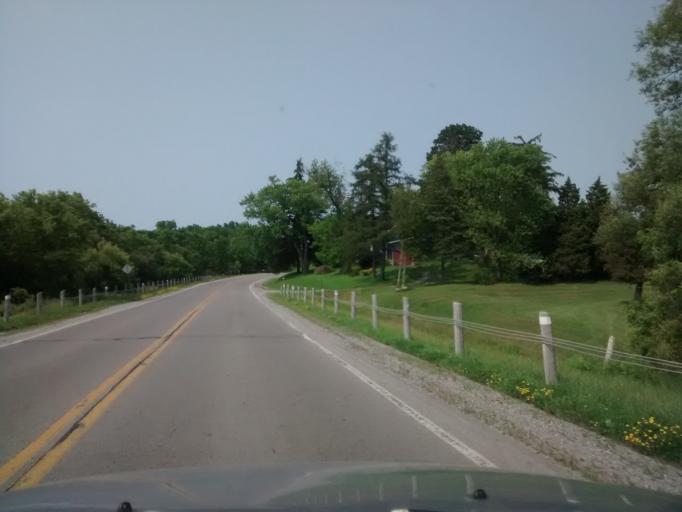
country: CA
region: Ontario
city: Ancaster
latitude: 42.9855
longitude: -79.8700
